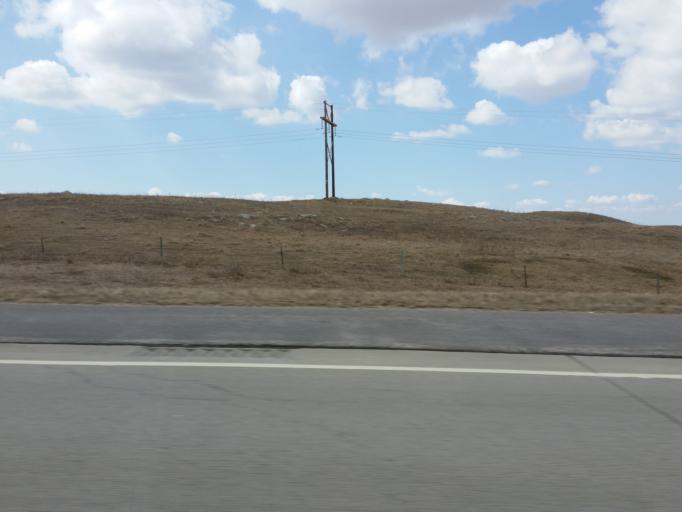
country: US
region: South Dakota
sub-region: Roberts County
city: Sisseton
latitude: 45.3727
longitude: -97.0499
